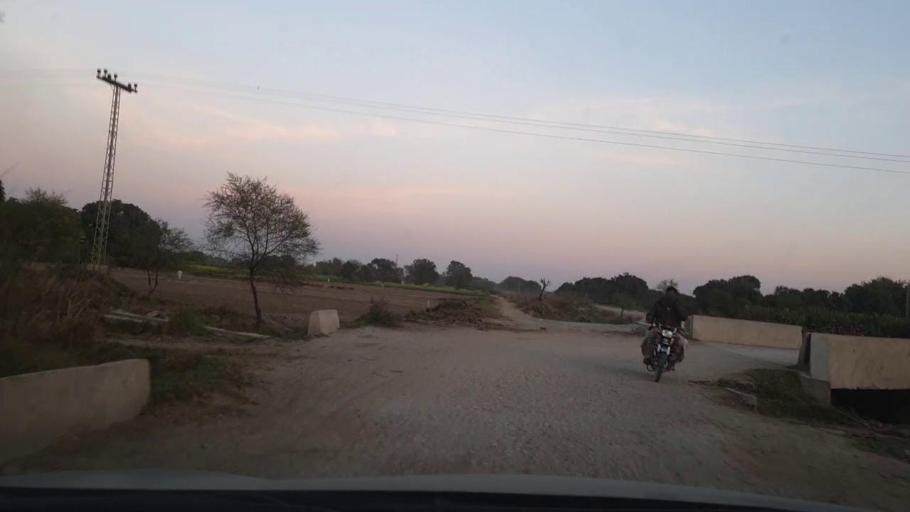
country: PK
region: Sindh
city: Tando Allahyar
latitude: 25.5549
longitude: 68.7886
